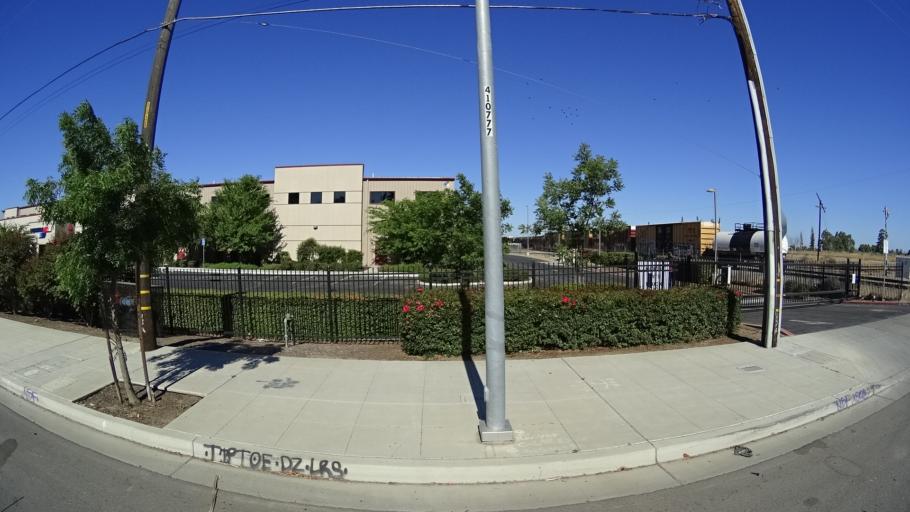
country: US
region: California
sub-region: Fresno County
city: West Park
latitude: 36.7461
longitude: -119.8356
